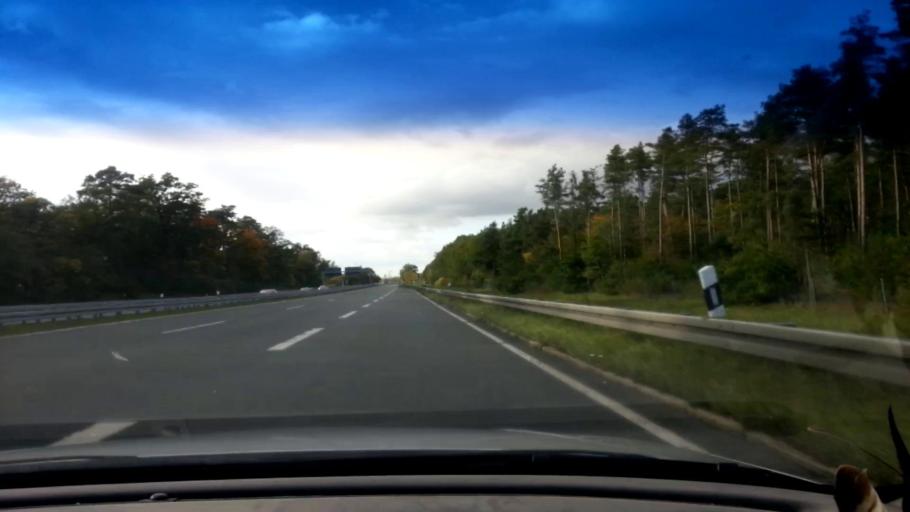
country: DE
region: Bavaria
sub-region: Upper Franconia
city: Bamberg
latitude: 49.8741
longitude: 10.9362
